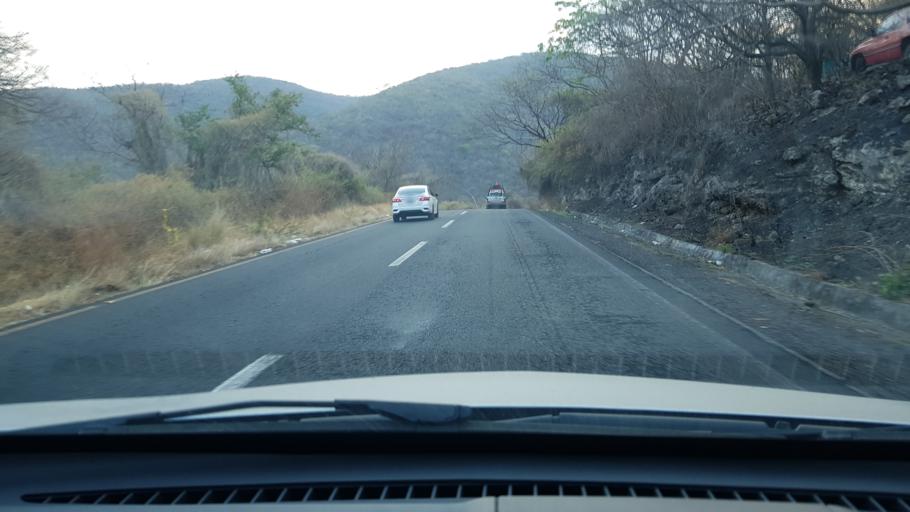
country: MX
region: Morelos
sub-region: Jiutepec
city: Independencia
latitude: 18.8569
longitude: -99.1091
